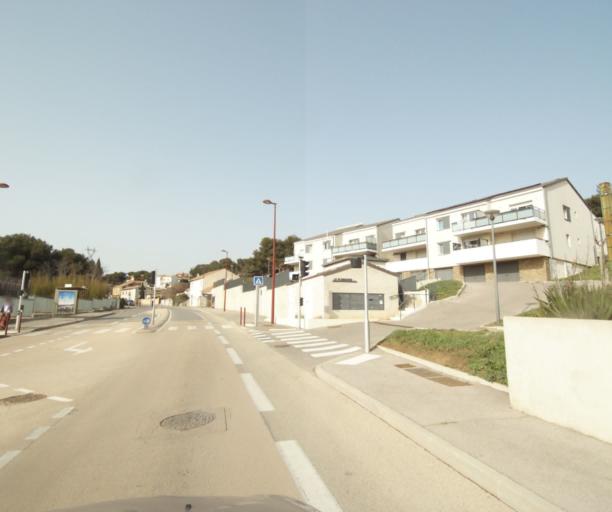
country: FR
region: Provence-Alpes-Cote d'Azur
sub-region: Departement des Bouches-du-Rhone
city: Septemes-les-Vallons
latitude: 43.4005
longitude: 5.3406
